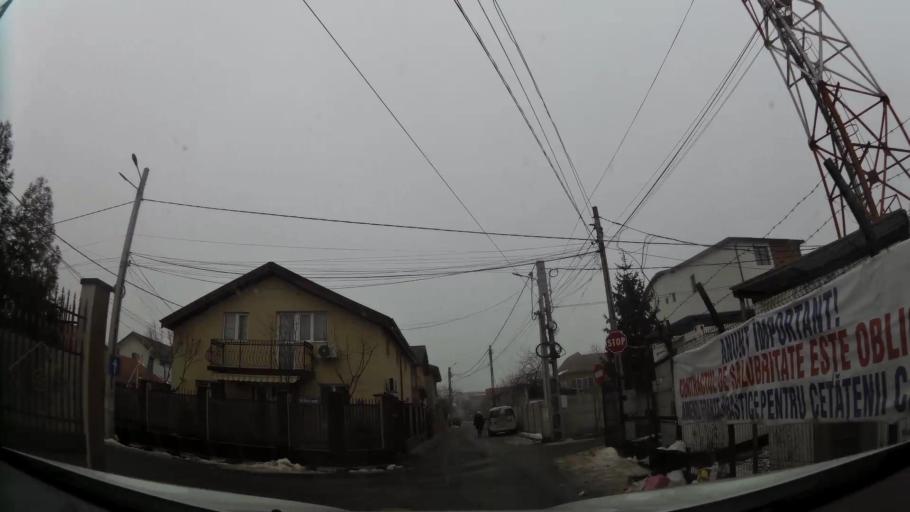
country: RO
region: Ilfov
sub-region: Comuna Chiajna
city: Rosu
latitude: 44.4475
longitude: 26.0101
